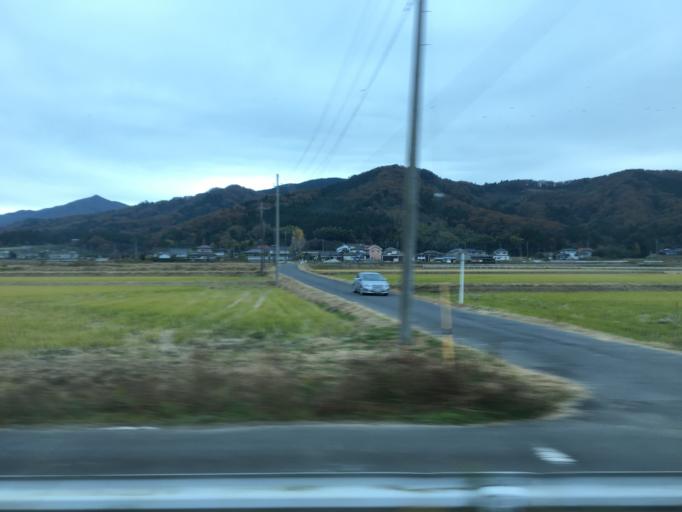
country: JP
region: Ibaraki
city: Iwase
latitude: 36.3573
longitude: 140.1265
